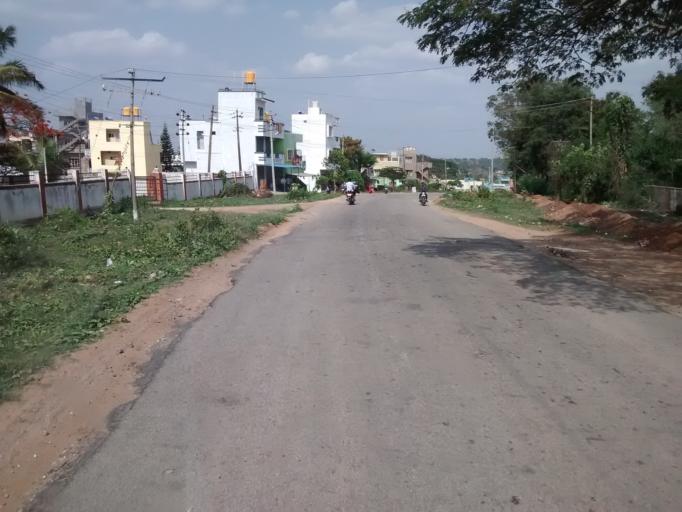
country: IN
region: Karnataka
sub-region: Mysore
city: Hunsur
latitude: 12.3361
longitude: 76.4506
